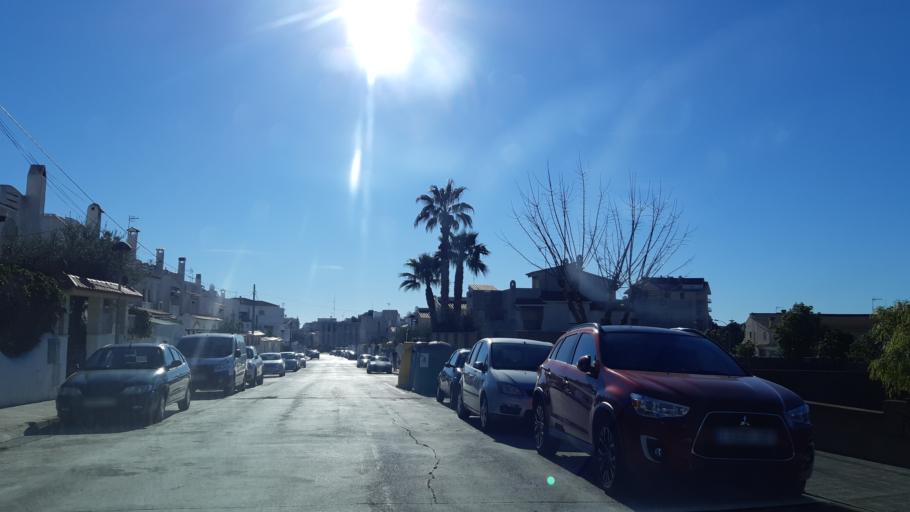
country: ES
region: Catalonia
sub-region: Provincia de Tarragona
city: Cunit
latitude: 41.2009
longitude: 1.6346
